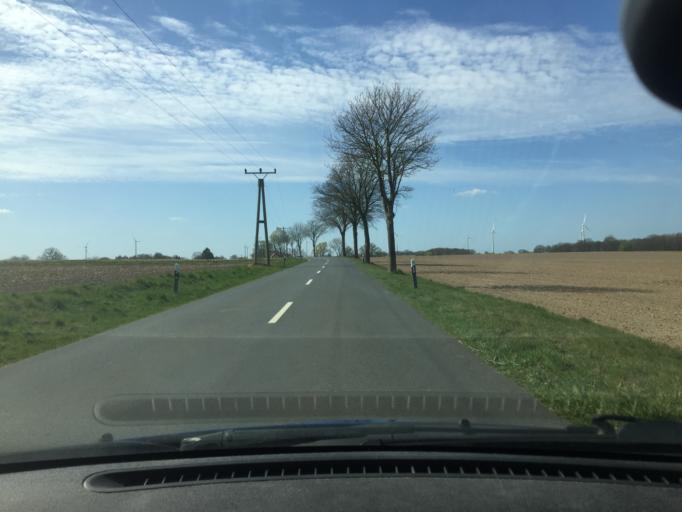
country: DE
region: Lower Saxony
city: Ratzlingen
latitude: 52.9662
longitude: 10.6744
